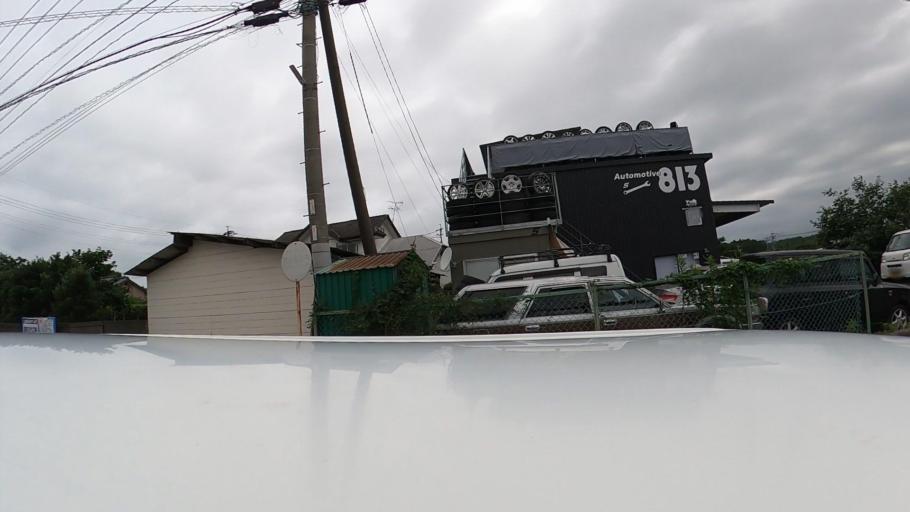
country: JP
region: Kumamoto
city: Ozu
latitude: 32.8363
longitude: 130.8752
